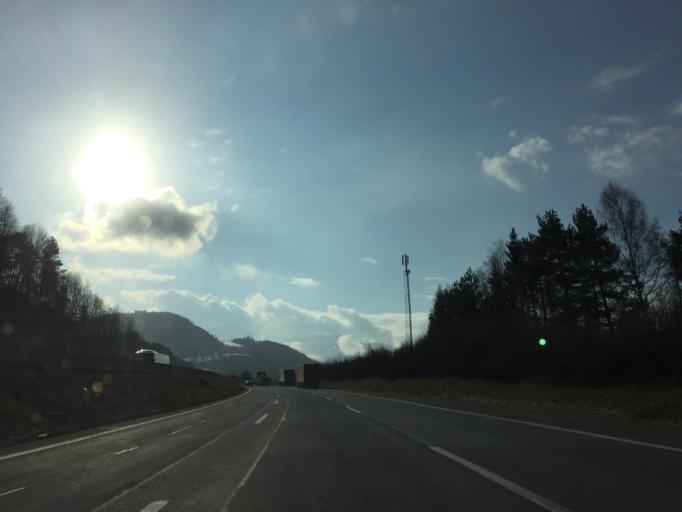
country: AT
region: Salzburg
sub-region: Politischer Bezirk Sankt Johann im Pongau
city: Pfarrwerfen
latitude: 47.4617
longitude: 13.2063
